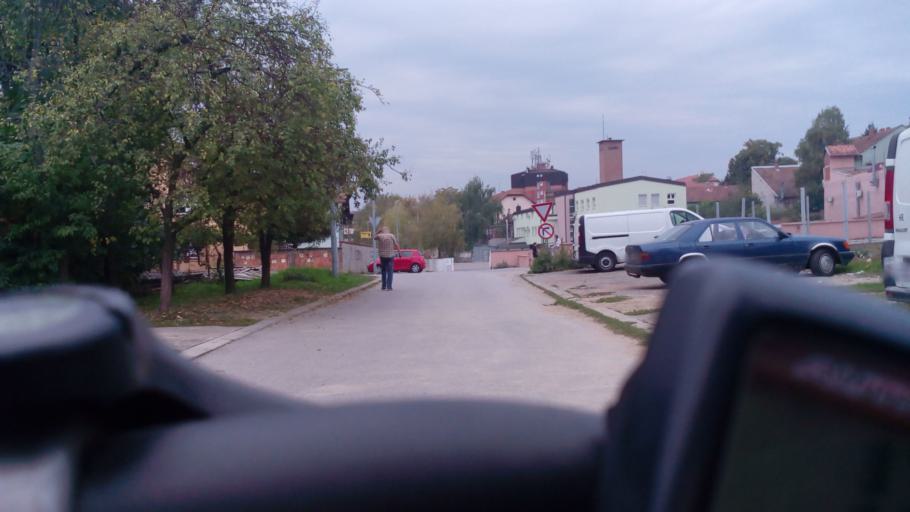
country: HR
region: Vukovarsko-Srijemska
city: Vinkovci
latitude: 45.2871
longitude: 18.8068
